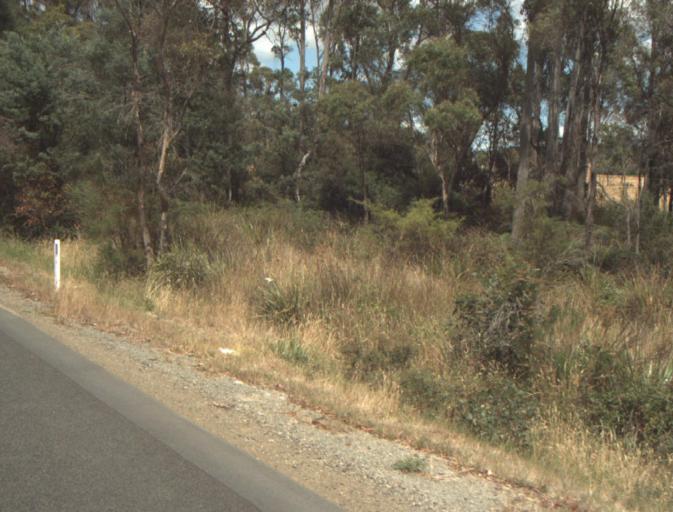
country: AU
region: Tasmania
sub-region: Launceston
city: Mayfield
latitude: -41.2298
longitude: 147.1449
